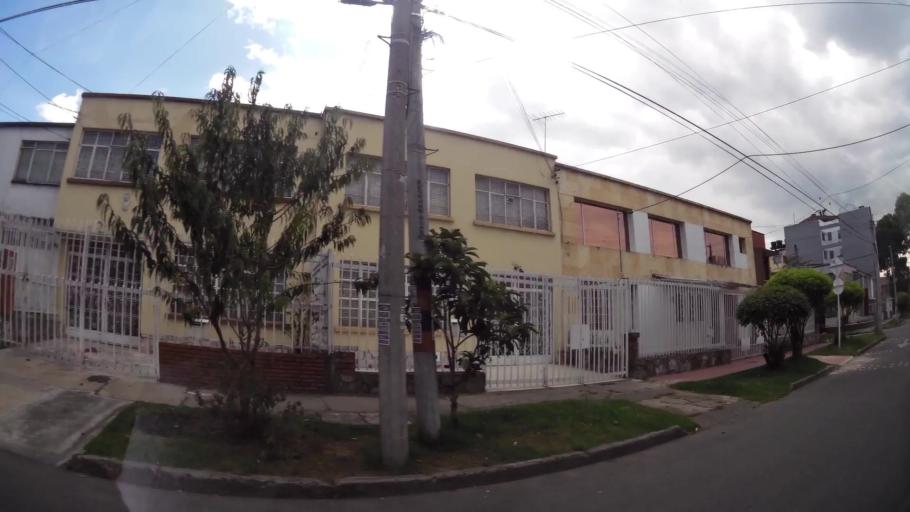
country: CO
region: Bogota D.C.
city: Bogota
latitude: 4.6501
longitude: -74.0752
